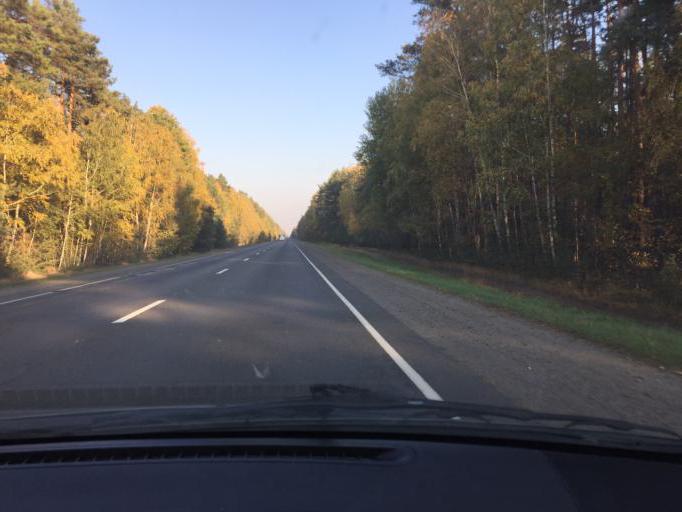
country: BY
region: Brest
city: Davyd-Haradok
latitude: 52.2384
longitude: 27.2804
